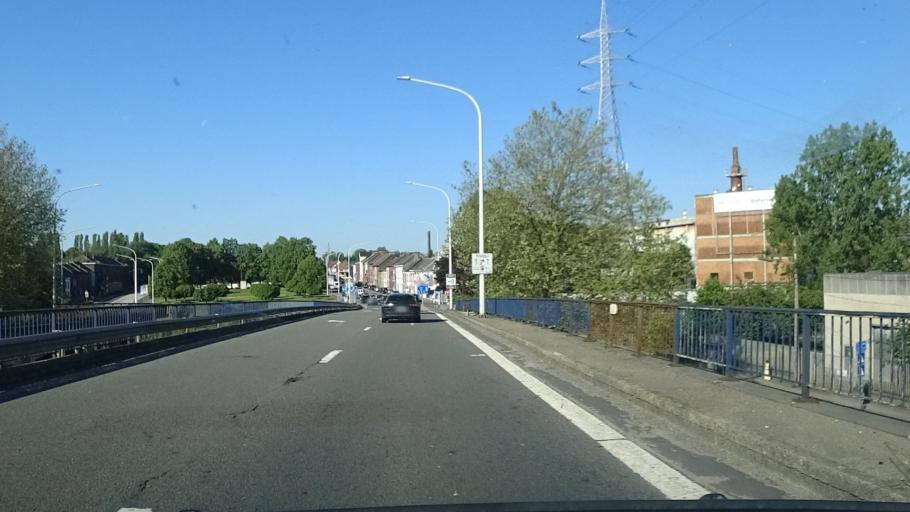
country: BE
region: Wallonia
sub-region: Province du Hainaut
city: La Louviere
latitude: 50.4911
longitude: 4.2043
